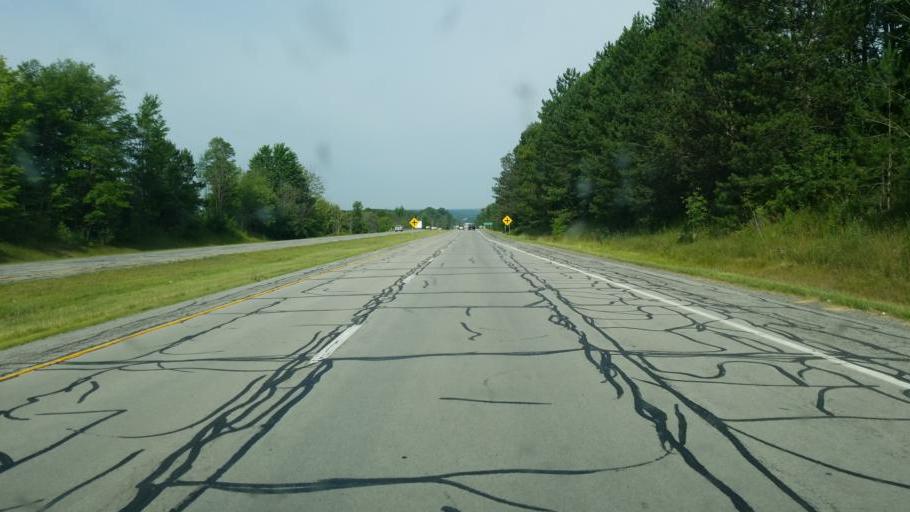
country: US
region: Ohio
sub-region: Medina County
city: Lodi
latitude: 41.0466
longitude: -81.9993
